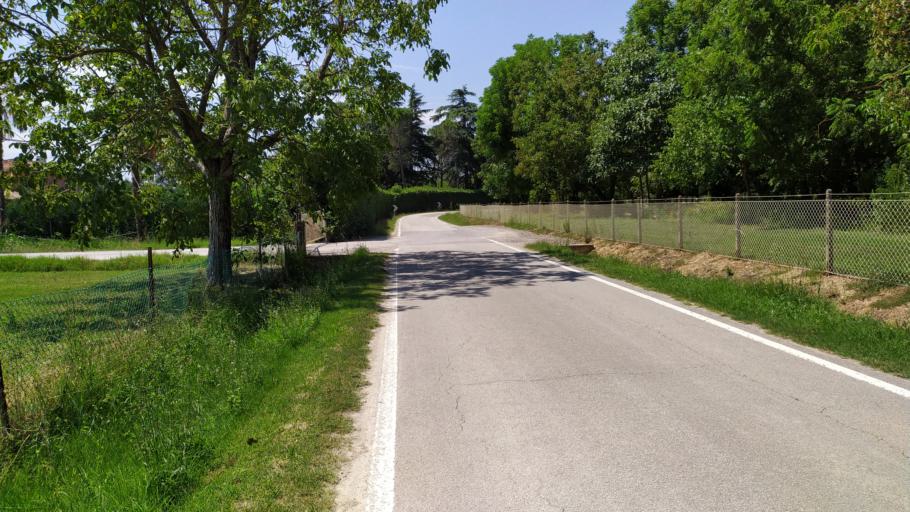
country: IT
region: Emilia-Romagna
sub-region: Forli-Cesena
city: Castrocaro Terme e Terra del Sole
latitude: 44.1998
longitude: 11.9838
